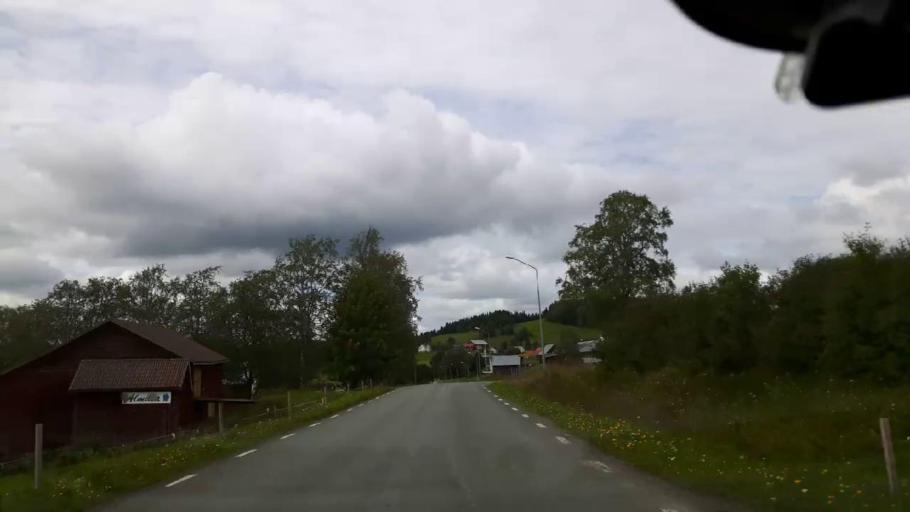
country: SE
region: Jaemtland
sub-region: Krokoms Kommun
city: Valla
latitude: 63.4863
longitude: 14.0400
